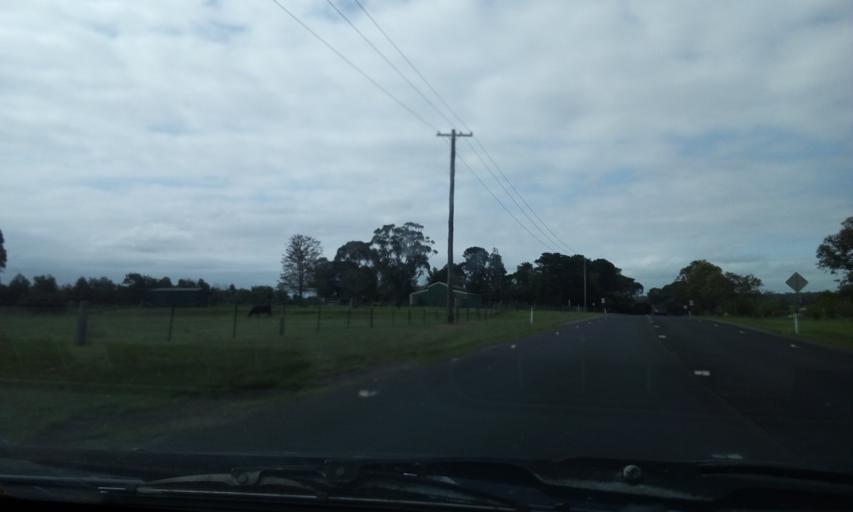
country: AU
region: New South Wales
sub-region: Campbelltown Municipality
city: Glen Alpine
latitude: -34.1134
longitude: 150.7436
